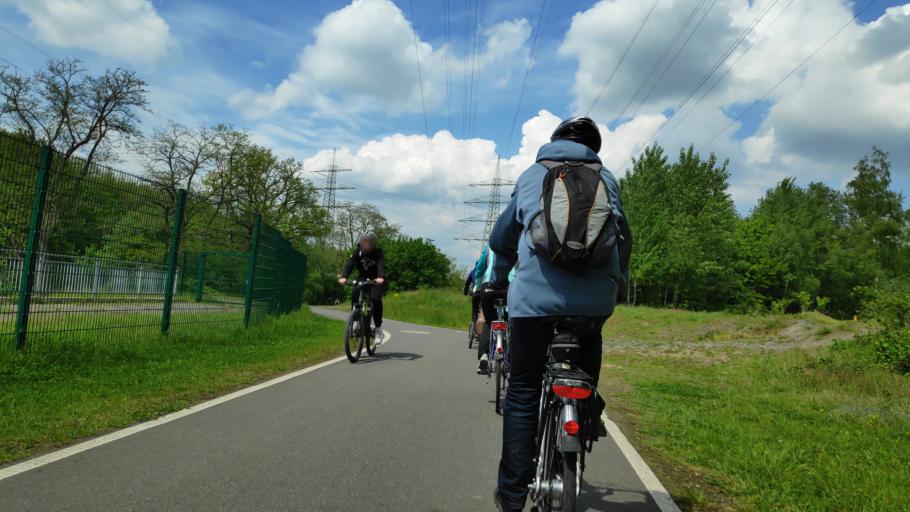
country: DE
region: North Rhine-Westphalia
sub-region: Regierungsbezirk Munster
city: Gelsenkirchen
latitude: 51.5359
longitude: 7.1307
